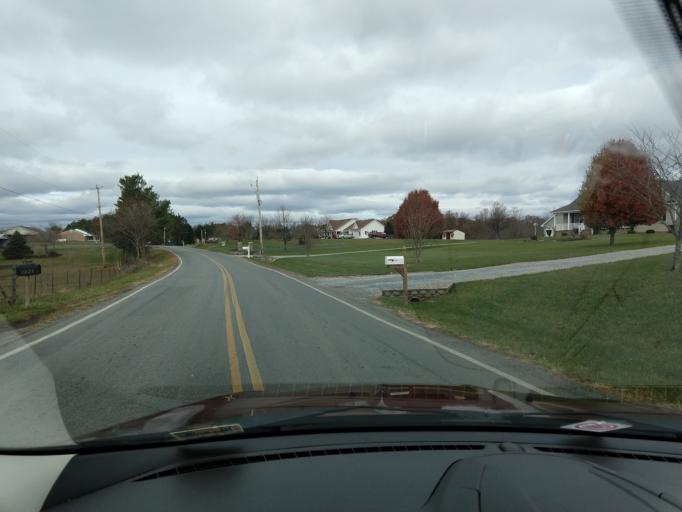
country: US
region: Virginia
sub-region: Franklin County
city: North Shore
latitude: 37.2375
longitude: -79.6727
